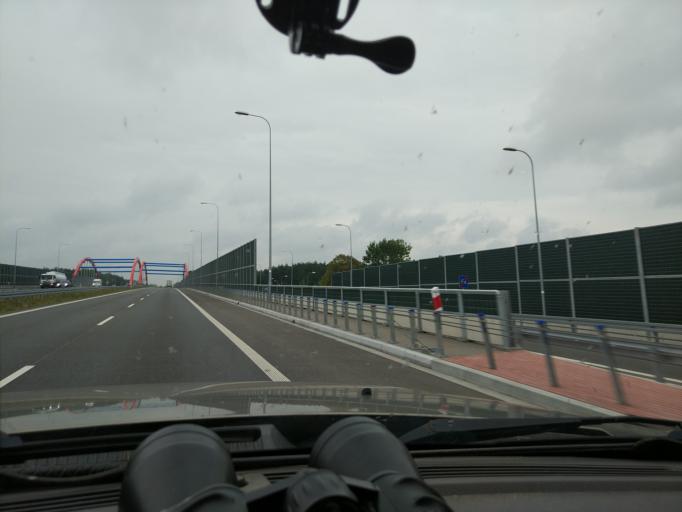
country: PL
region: Masovian Voivodeship
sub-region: Powiat ostrowski
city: Ostrow Mazowiecka
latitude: 52.8265
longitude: 21.9362
